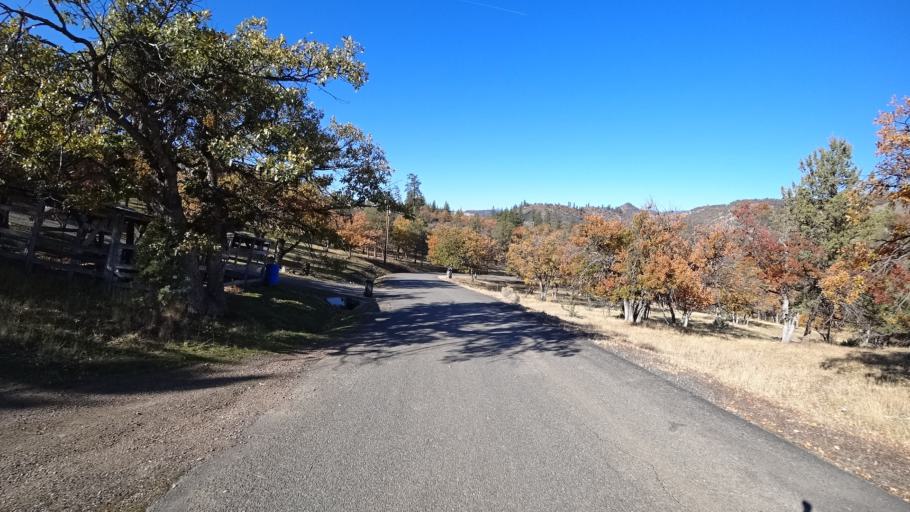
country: US
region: California
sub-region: Siskiyou County
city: Montague
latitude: 41.9775
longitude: -122.3249
